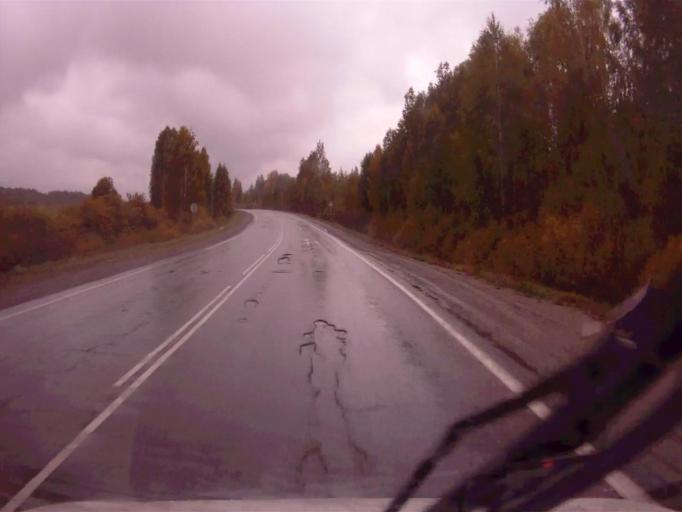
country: RU
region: Chelyabinsk
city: Argayash
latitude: 55.4862
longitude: 60.7371
